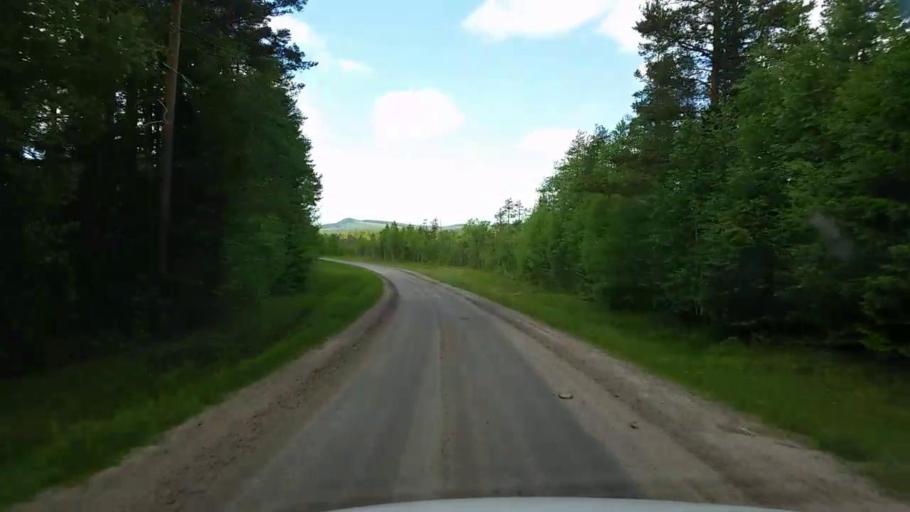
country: SE
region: Gaevleborg
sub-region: Ovanakers Kommun
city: Edsbyn
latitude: 61.5695
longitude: 15.9518
